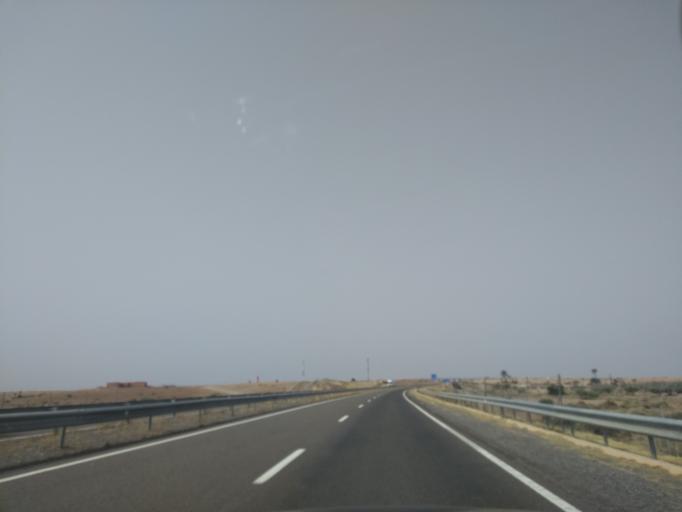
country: MA
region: Marrakech-Tensift-Al Haouz
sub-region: Marrakech
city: Marrakesh
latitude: 31.7277
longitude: -8.2214
